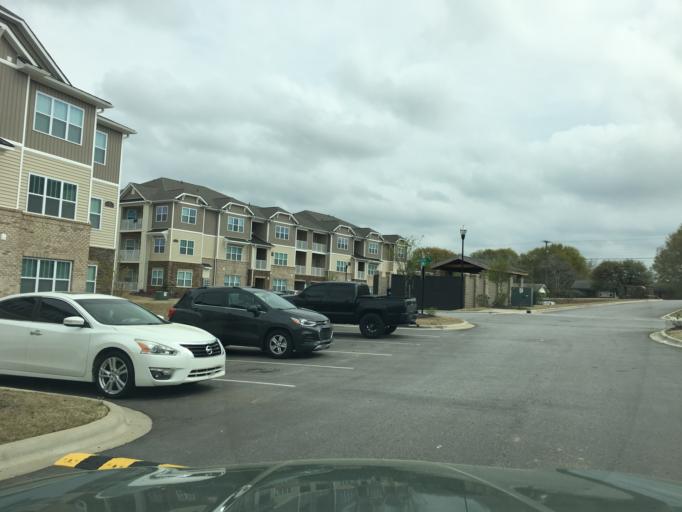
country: US
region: South Carolina
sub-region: Greenville County
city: Greer
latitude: 34.9284
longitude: -82.2435
